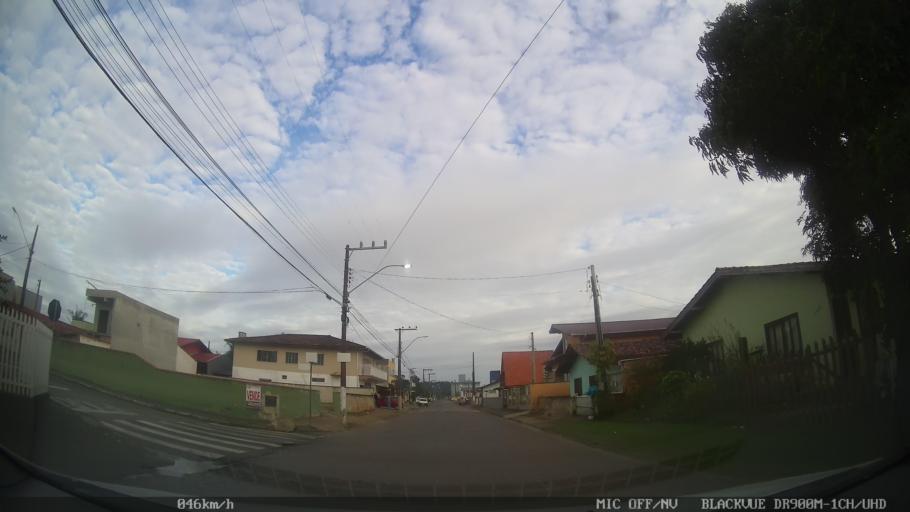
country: BR
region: Santa Catarina
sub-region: Barra Velha
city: Barra Velha
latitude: -26.6295
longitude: -48.6911
